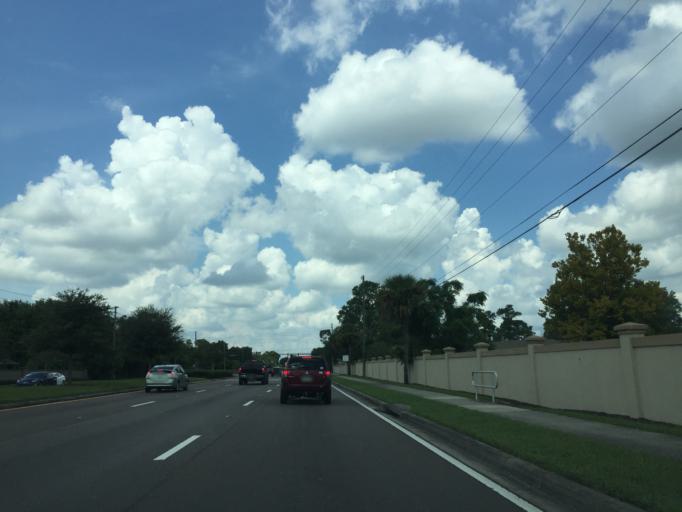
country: US
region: Florida
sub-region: Seminole County
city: Goldenrod
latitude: 28.6479
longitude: -81.2562
